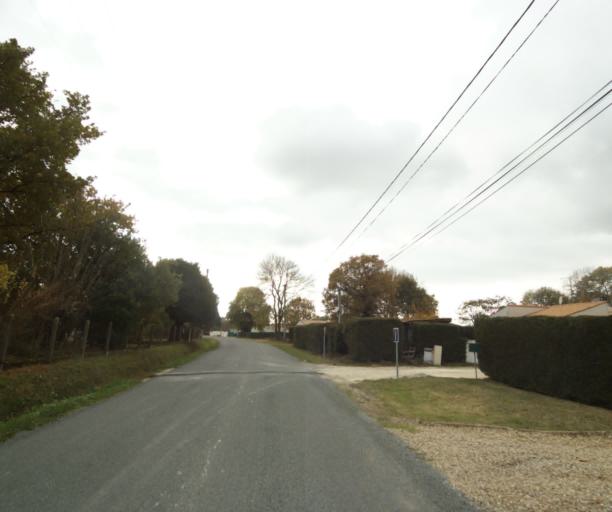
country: FR
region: Poitou-Charentes
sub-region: Departement de la Charente-Maritime
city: Saint-Georges-des-Coteaux
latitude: 45.7805
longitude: -0.6998
